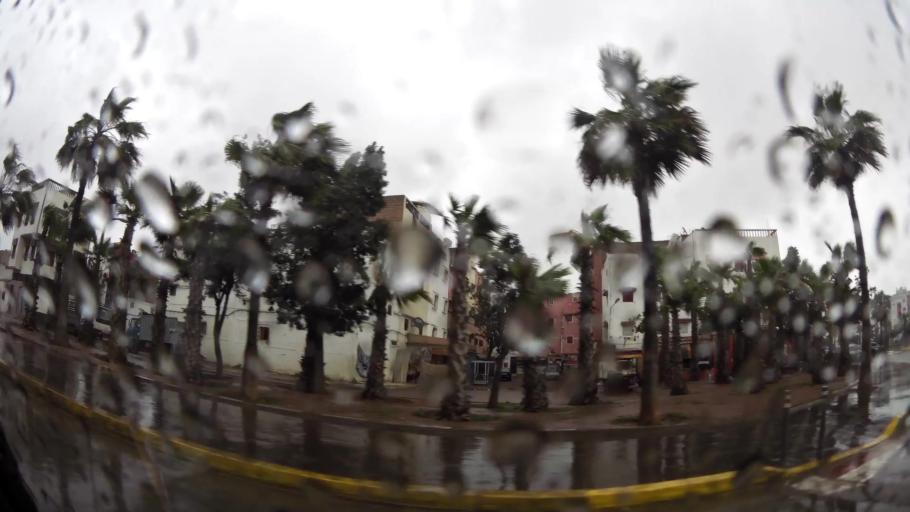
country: MA
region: Grand Casablanca
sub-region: Mediouna
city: Tit Mellil
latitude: 33.5519
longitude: -7.5523
